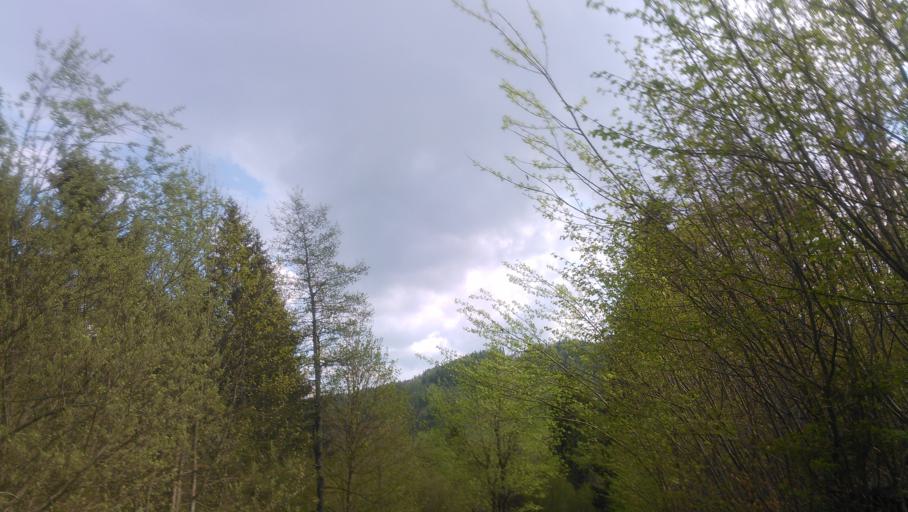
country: SK
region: Banskobystricky
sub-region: Okres Banska Bystrica
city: Brezno
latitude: 48.8761
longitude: 19.5901
